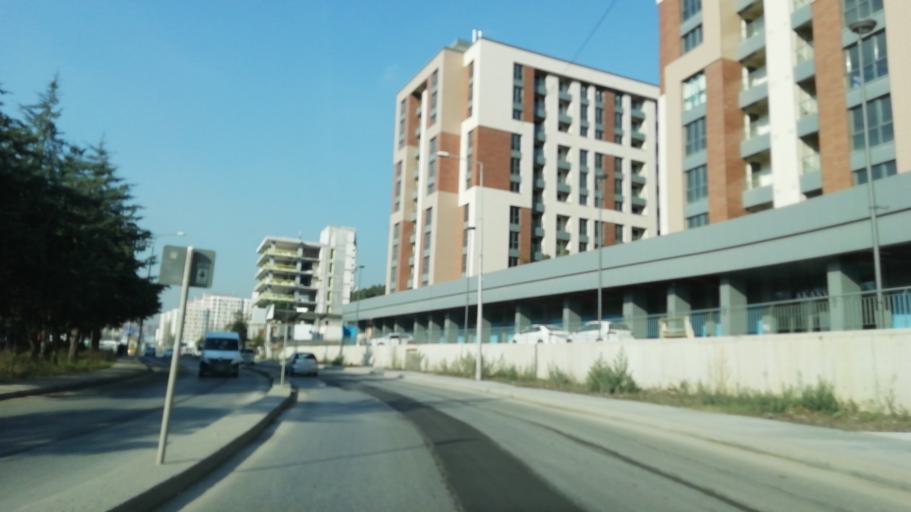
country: TR
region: Istanbul
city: Sisli
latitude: 41.0877
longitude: 28.9488
